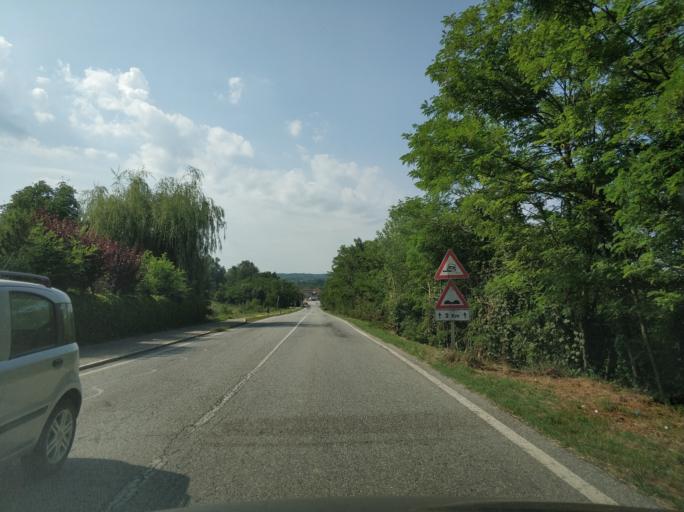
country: IT
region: Piedmont
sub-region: Provincia di Torino
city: Pralormo
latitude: 44.8678
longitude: 7.8963
